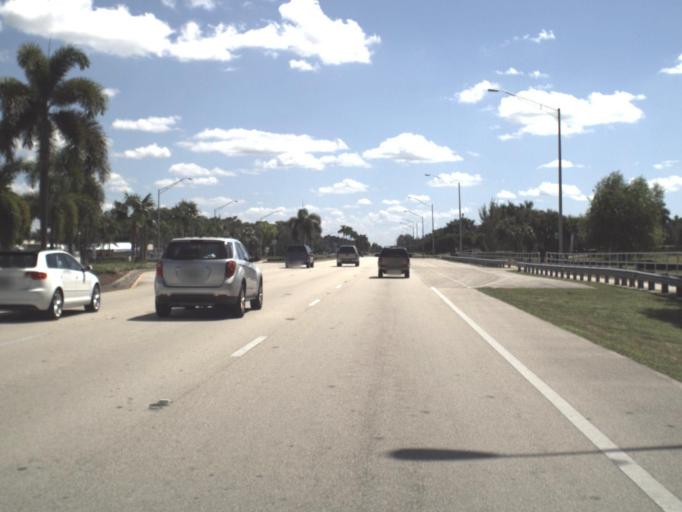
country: US
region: Florida
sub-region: Collier County
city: Lely
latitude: 26.0960
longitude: -81.7379
